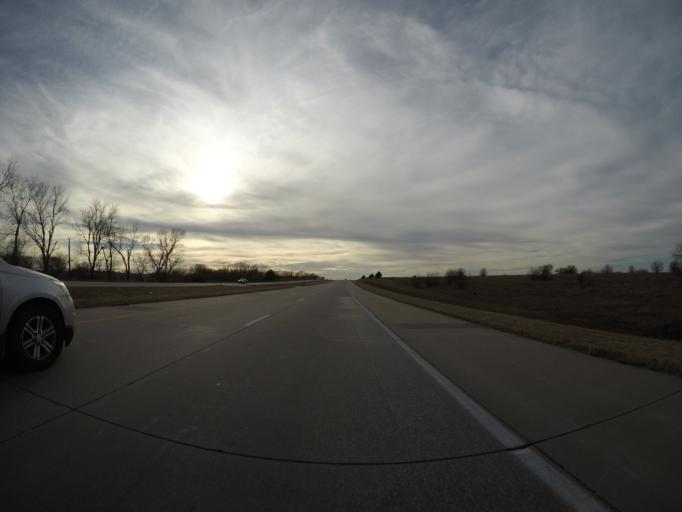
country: US
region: Kansas
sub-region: Franklin County
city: Ottawa
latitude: 38.5022
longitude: -95.4388
